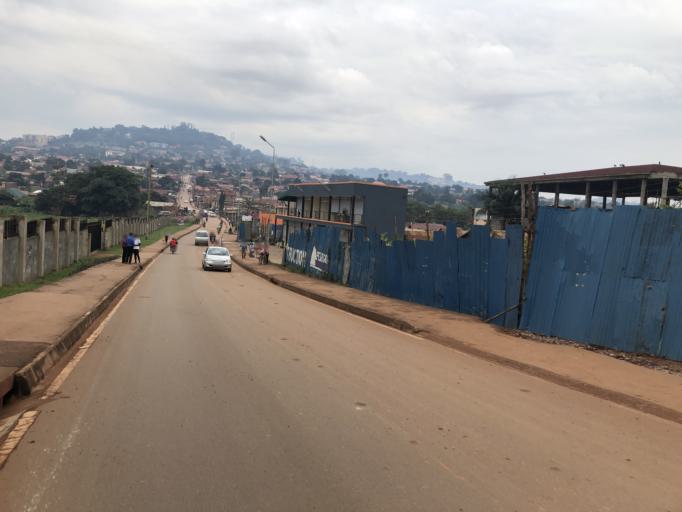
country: UG
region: Central Region
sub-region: Kampala District
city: Kampala
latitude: 0.2846
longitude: 32.6054
